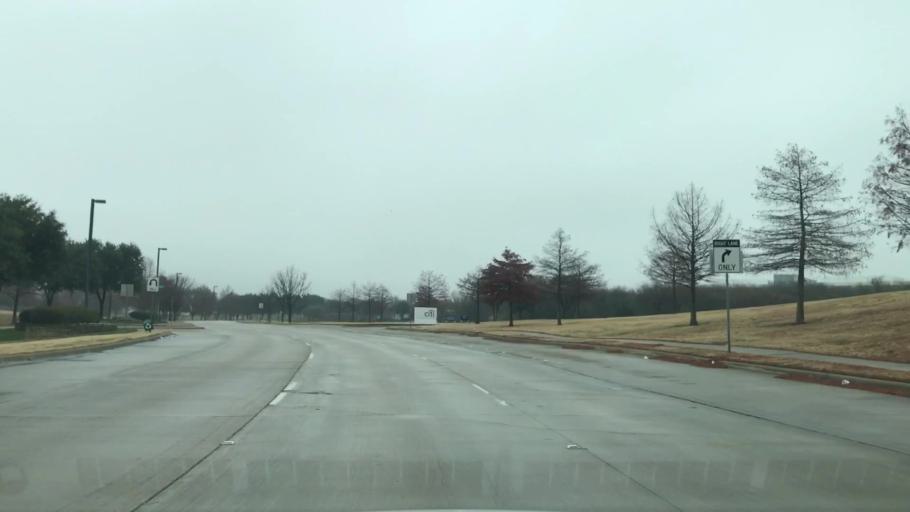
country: US
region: Texas
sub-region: Dallas County
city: Farmers Branch
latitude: 32.8979
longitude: -96.9517
